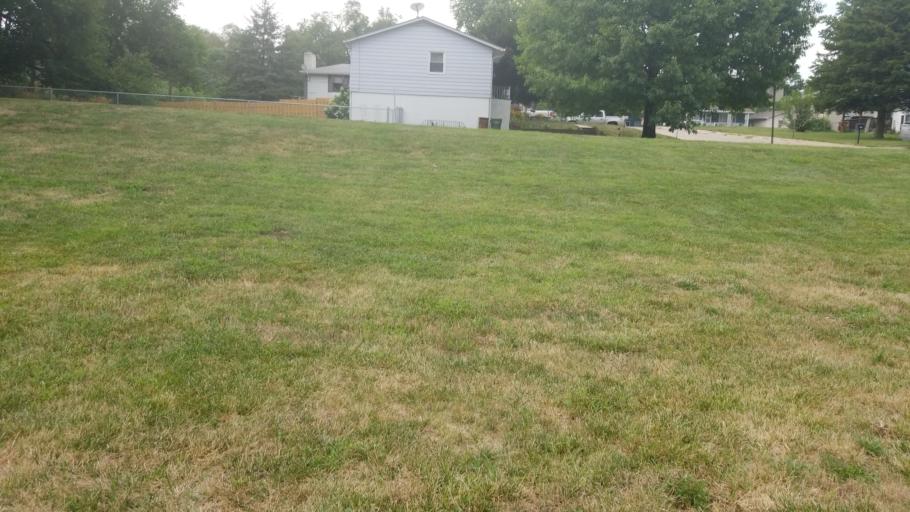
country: US
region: Nebraska
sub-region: Sarpy County
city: Bellevue
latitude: 41.1280
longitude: -95.9006
